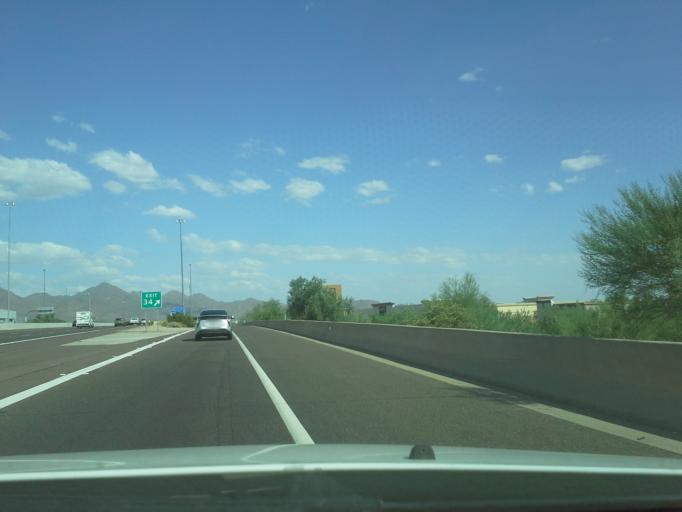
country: US
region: Arizona
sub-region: Maricopa County
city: Paradise Valley
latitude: 33.6591
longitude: -111.9306
